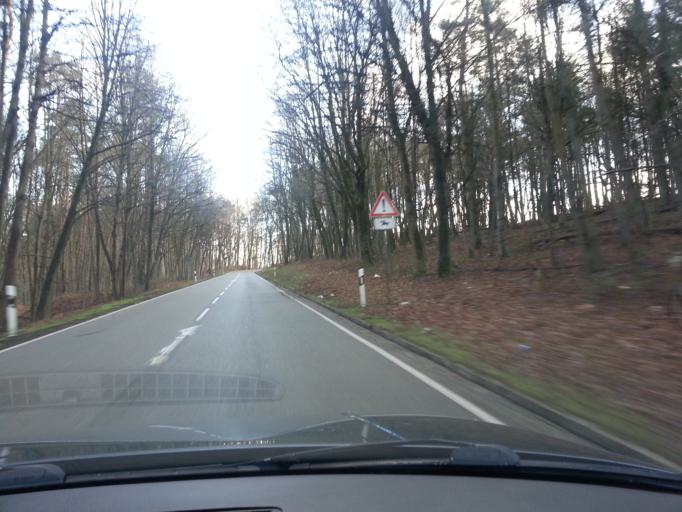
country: DE
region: Rheinland-Pfalz
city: Rodenbach
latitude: 49.4701
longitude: 7.6754
